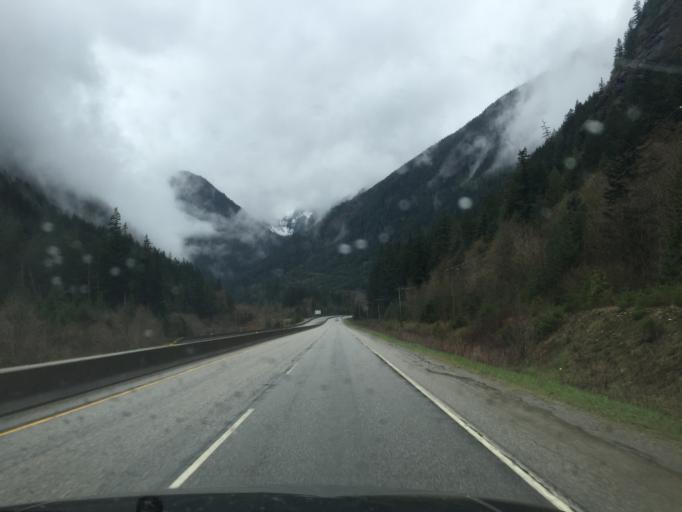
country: CA
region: British Columbia
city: Hope
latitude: 49.4410
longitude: -121.2849
